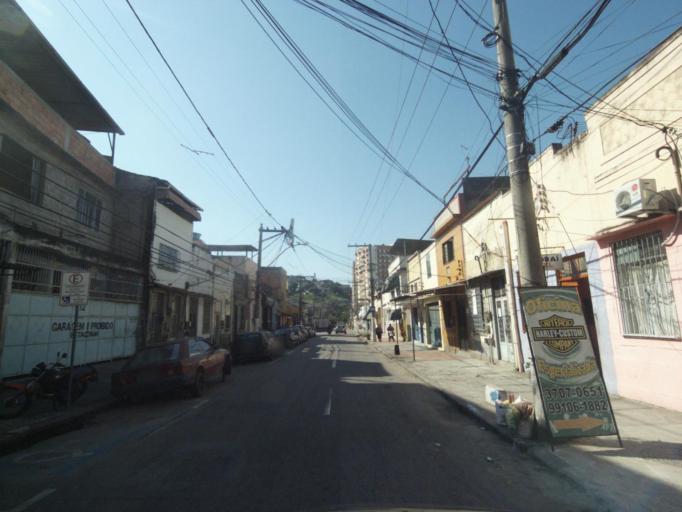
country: BR
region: Rio de Janeiro
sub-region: Niteroi
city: Niteroi
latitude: -22.8841
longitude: -43.1225
